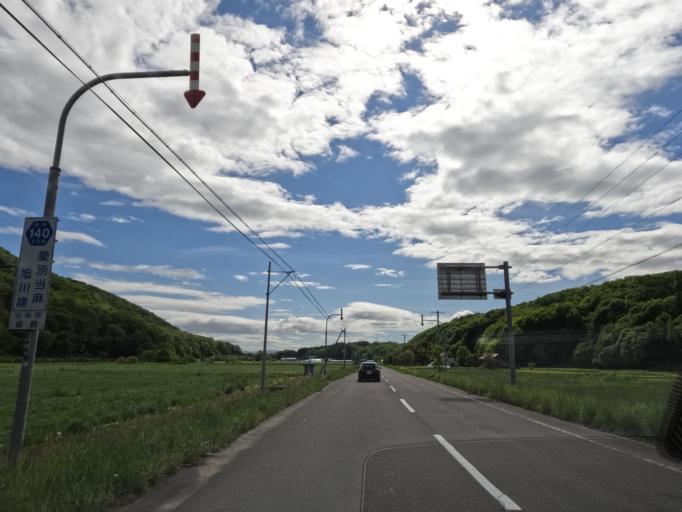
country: JP
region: Hokkaido
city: Kamikawa
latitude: 43.8711
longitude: 142.5740
